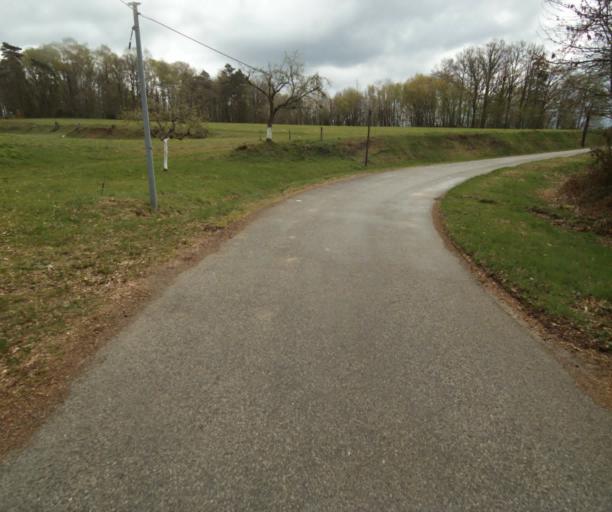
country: FR
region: Limousin
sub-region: Departement de la Correze
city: Laguenne
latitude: 45.2364
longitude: 1.8912
